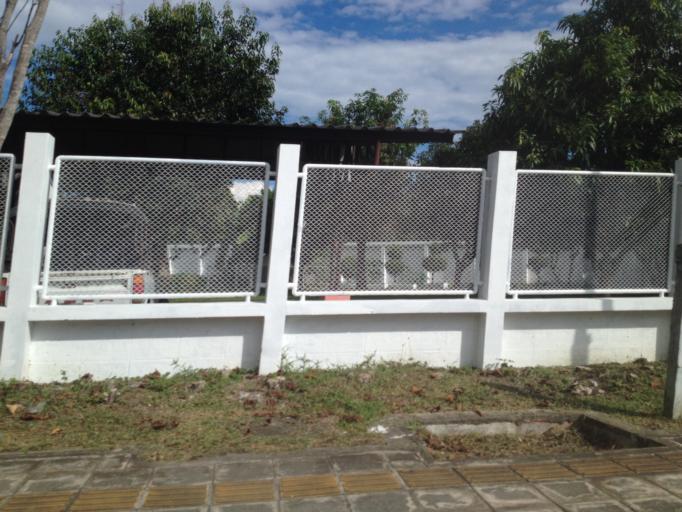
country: TH
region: Chiang Mai
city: Chiang Mai
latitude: 18.7713
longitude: 98.9690
